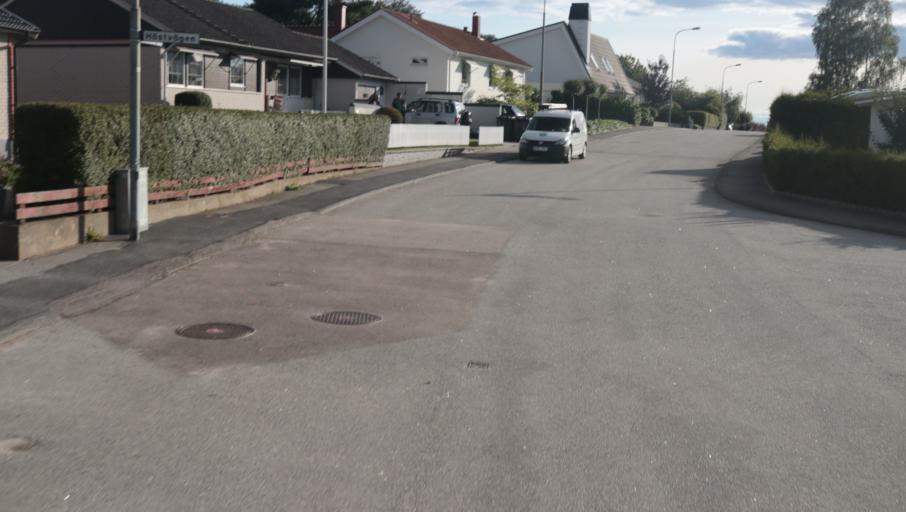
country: SE
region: Blekinge
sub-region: Karlshamns Kommun
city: Karlshamn
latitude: 56.1653
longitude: 14.8945
